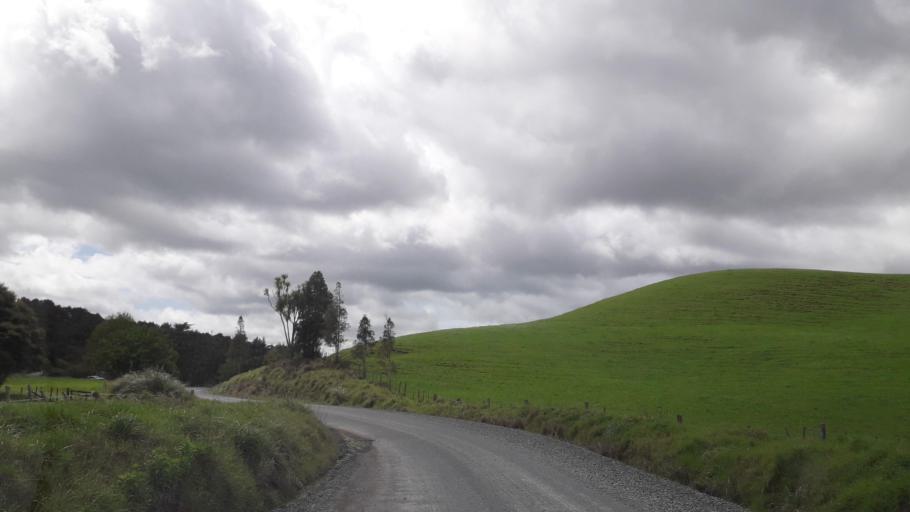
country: NZ
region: Northland
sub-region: Far North District
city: Kaitaia
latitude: -35.1733
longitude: 173.3298
